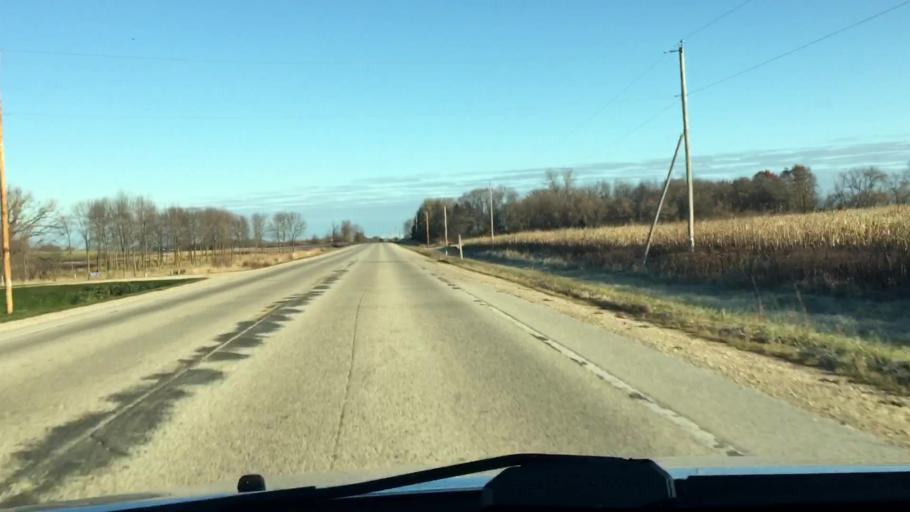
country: US
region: Wisconsin
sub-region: Dodge County
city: Theresa
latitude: 43.4902
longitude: -88.4501
